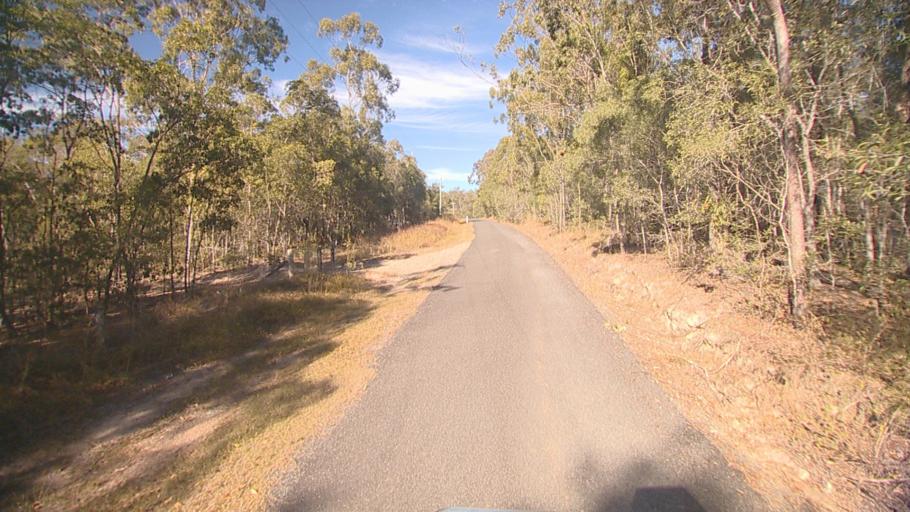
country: AU
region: Queensland
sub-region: Logan
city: Windaroo
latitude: -27.7911
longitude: 153.1711
